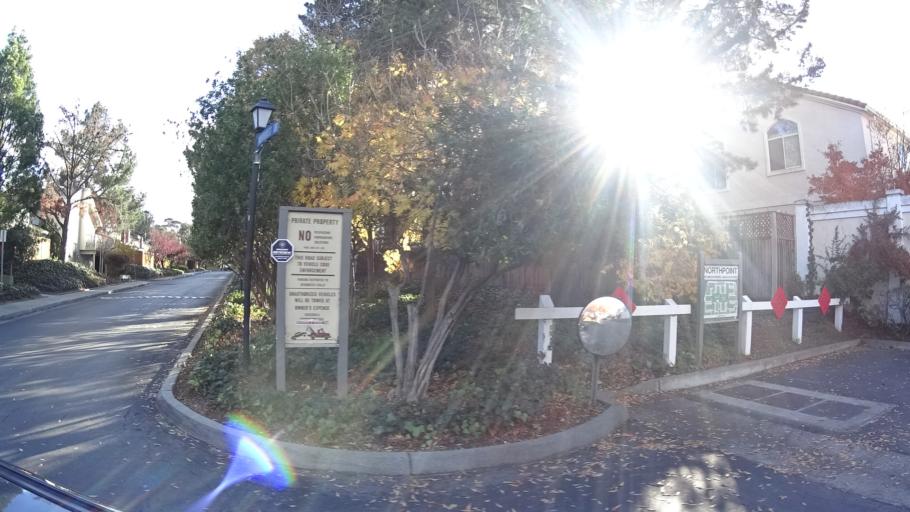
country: US
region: California
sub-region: Santa Clara County
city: Cupertino
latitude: 37.3364
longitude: -122.0291
